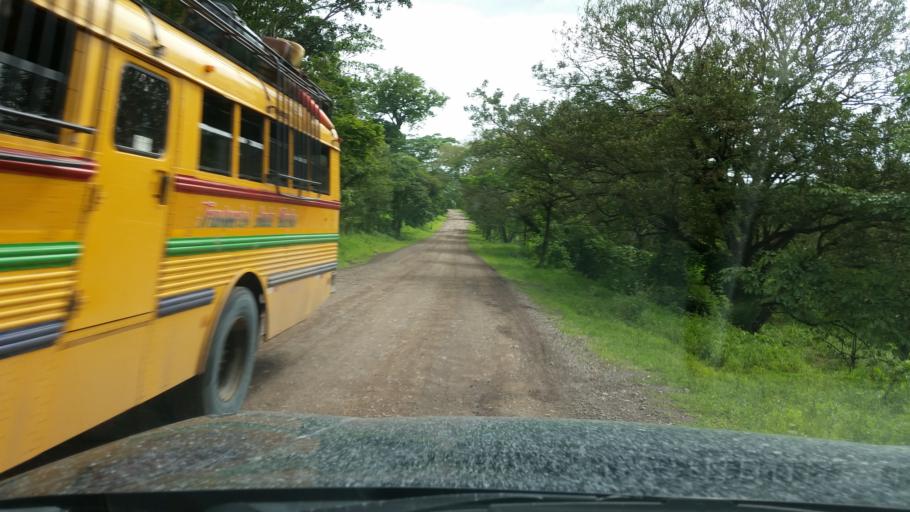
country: NI
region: Atlantico Norte (RAAN)
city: Siuna
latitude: 13.5236
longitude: -84.8280
